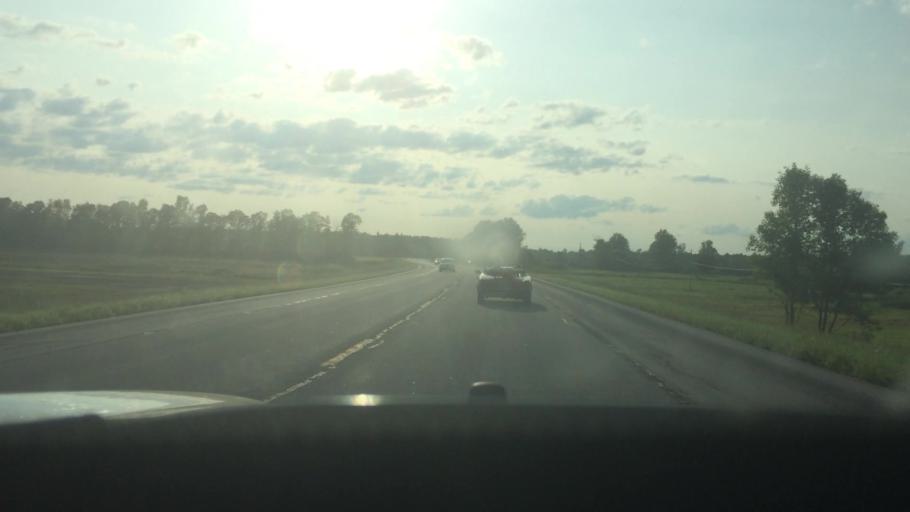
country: US
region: New York
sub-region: St. Lawrence County
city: Canton
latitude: 44.6357
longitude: -75.2630
